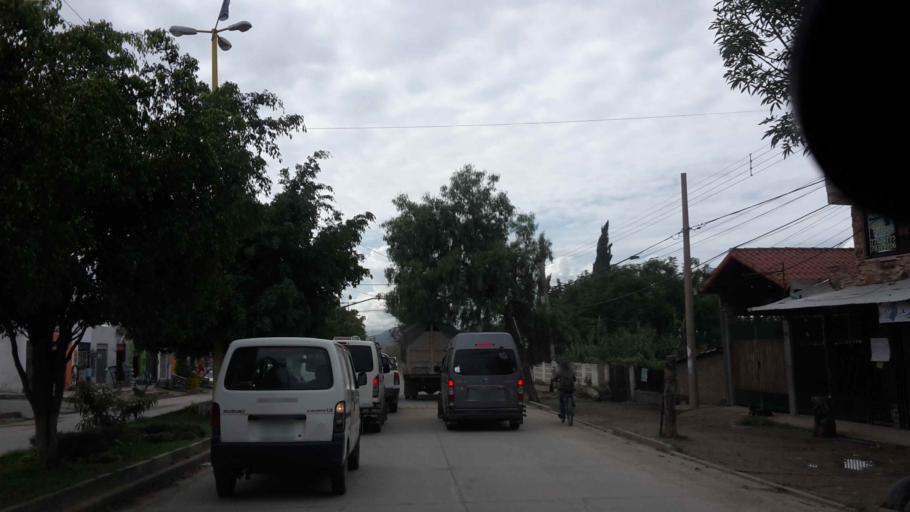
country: BO
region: Cochabamba
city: Cochabamba
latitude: -17.3497
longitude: -66.1963
